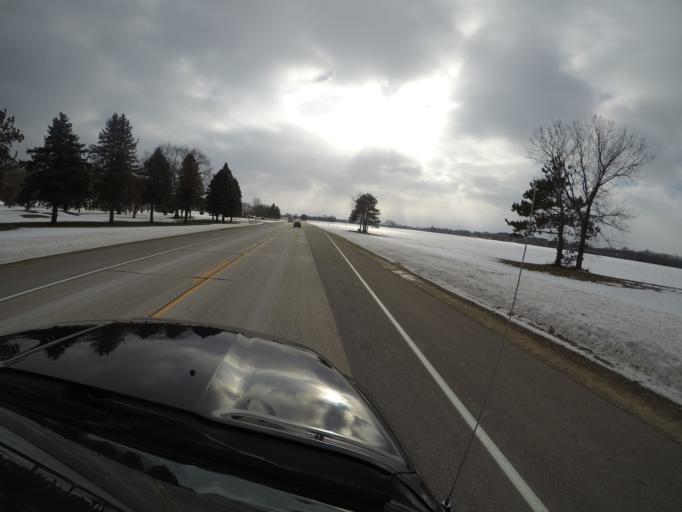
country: US
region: Wisconsin
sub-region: Trempealeau County
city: Galesville
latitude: 44.0324
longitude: -91.2907
